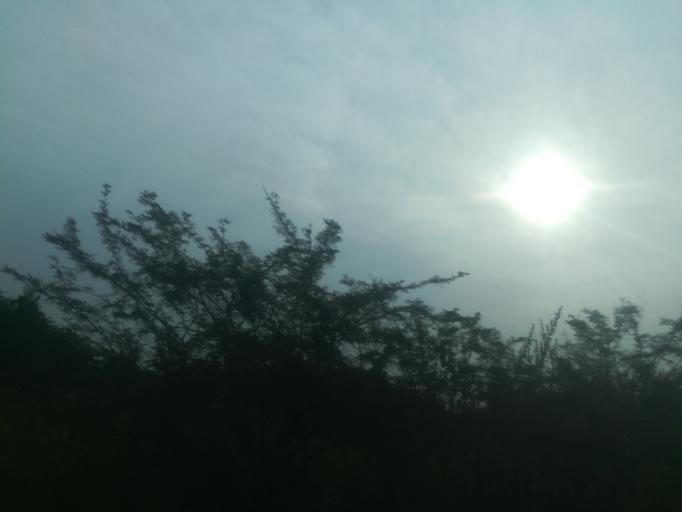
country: NG
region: Ogun
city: Ayetoro
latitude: 7.2695
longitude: 3.1044
